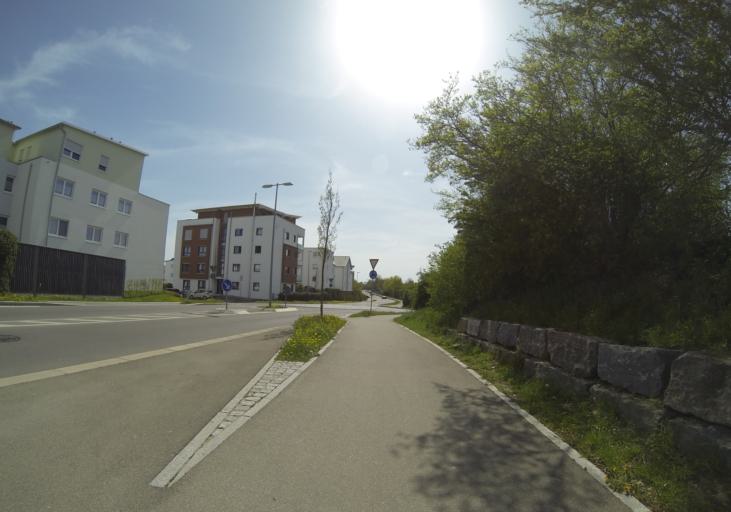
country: DE
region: Baden-Wuerttemberg
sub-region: Tuebingen Region
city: Achstetten
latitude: 48.2412
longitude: 9.8947
